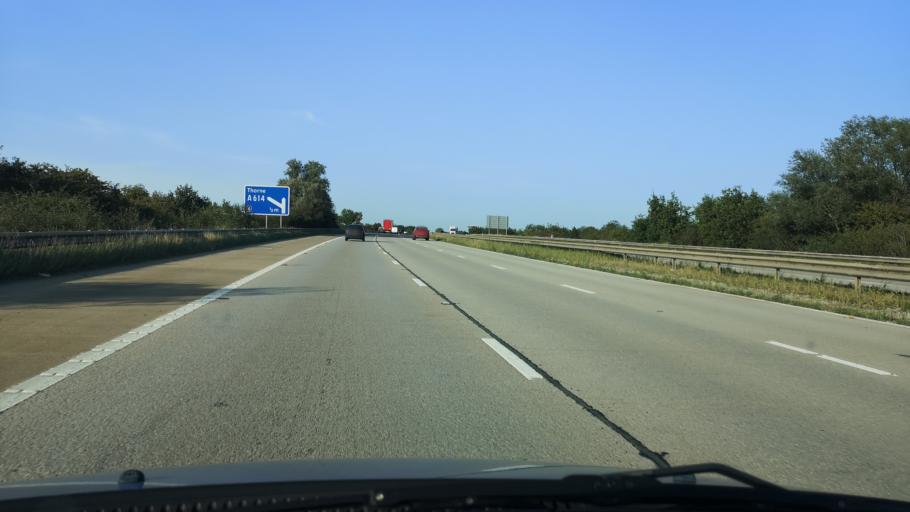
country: GB
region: England
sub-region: Doncaster
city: Hatfield
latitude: 53.6078
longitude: -0.9900
